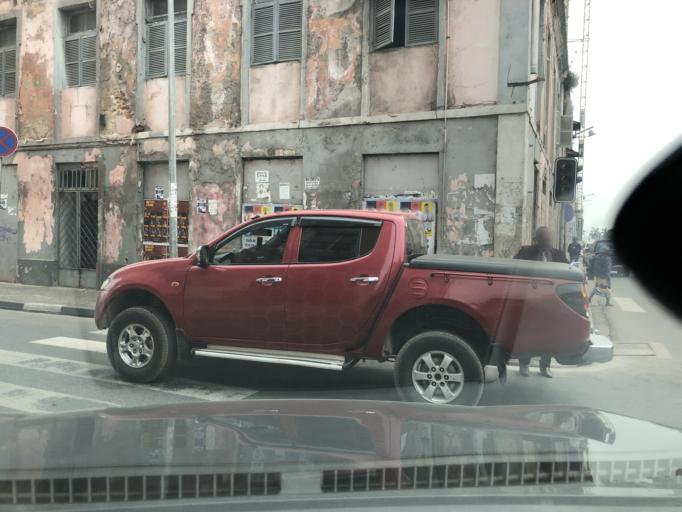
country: AO
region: Luanda
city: Luanda
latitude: -8.8129
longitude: 13.2326
